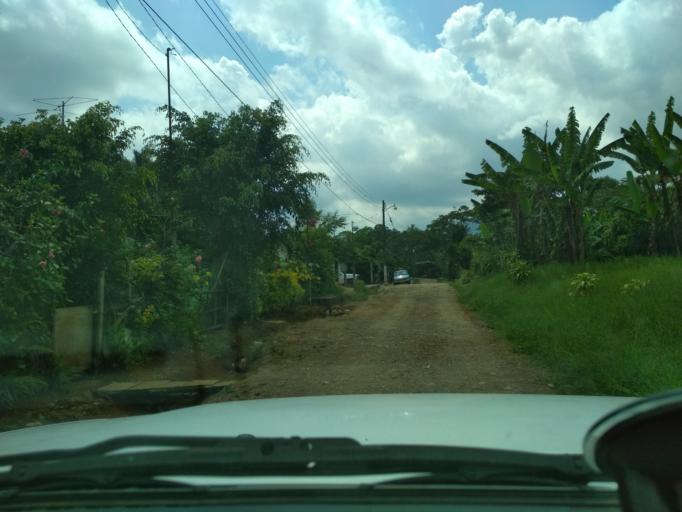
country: MX
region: Veracruz
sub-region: Fortin
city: Monte Salas
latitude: 18.9374
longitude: -97.0133
